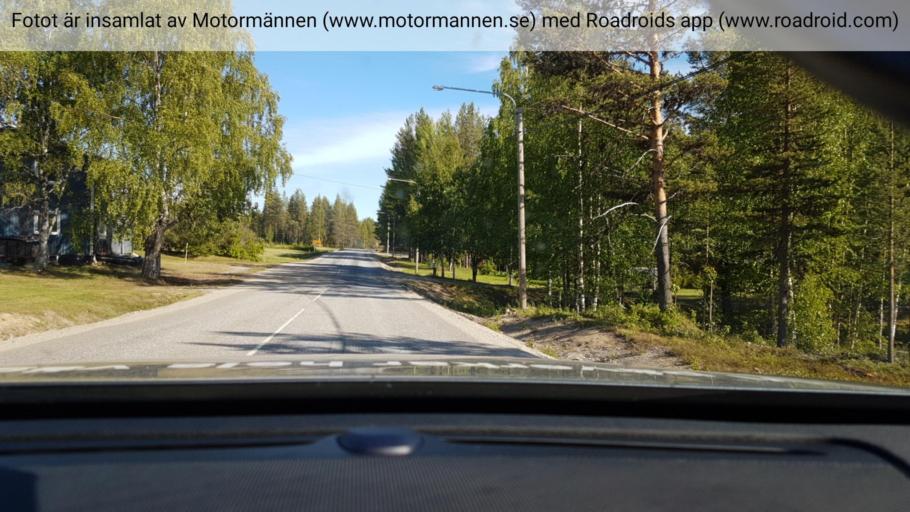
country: SE
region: Vaesterbotten
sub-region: Norsjo Kommun
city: Norsjoe
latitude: 64.7034
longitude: 19.1596
